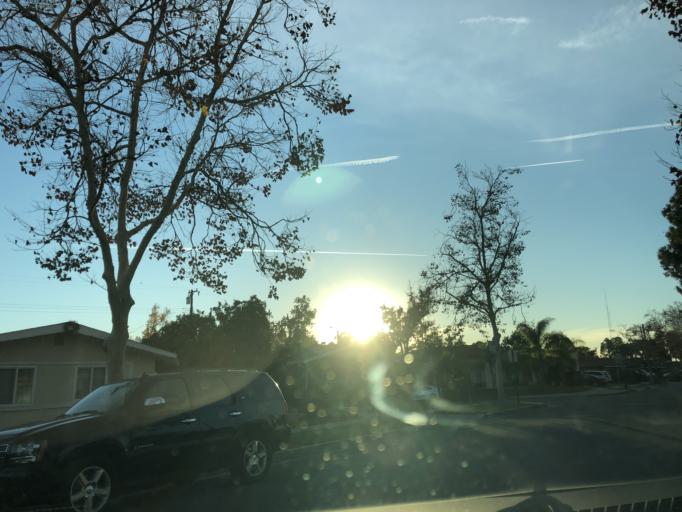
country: US
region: California
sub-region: Orange County
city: Tustin
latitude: 33.7574
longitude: -117.8461
